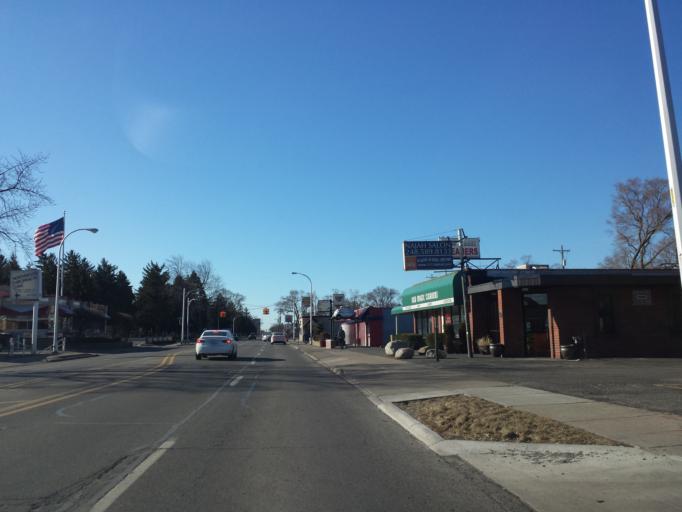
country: US
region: Michigan
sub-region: Oakland County
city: Royal Oak
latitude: 42.5054
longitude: -83.1451
